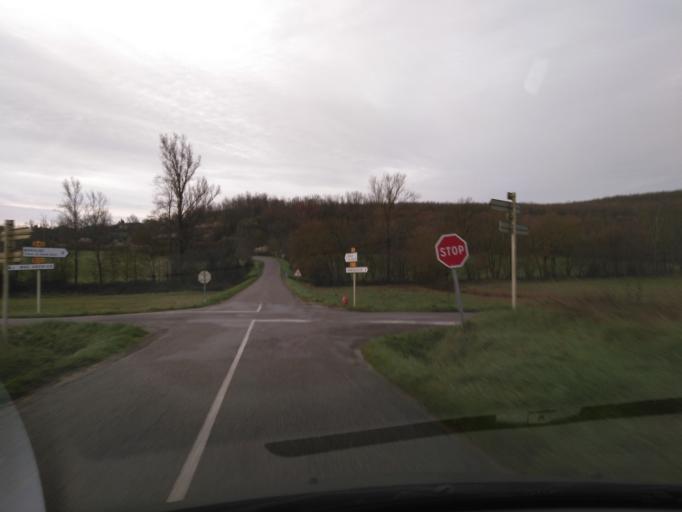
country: FR
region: Midi-Pyrenees
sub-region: Departement du Tarn-et-Garonne
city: Finhan
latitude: 43.8803
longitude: 1.1455
